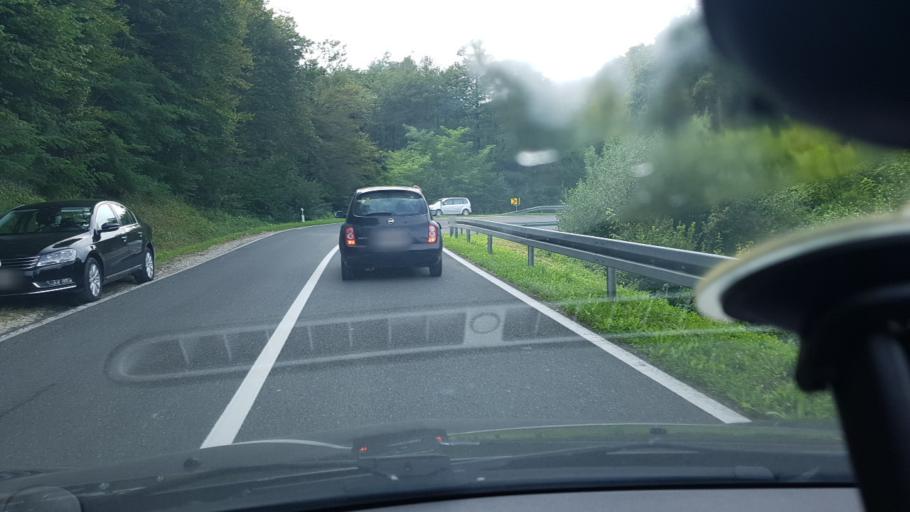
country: HR
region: Varazdinska
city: Ljubescica
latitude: 46.1404
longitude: 16.3603
